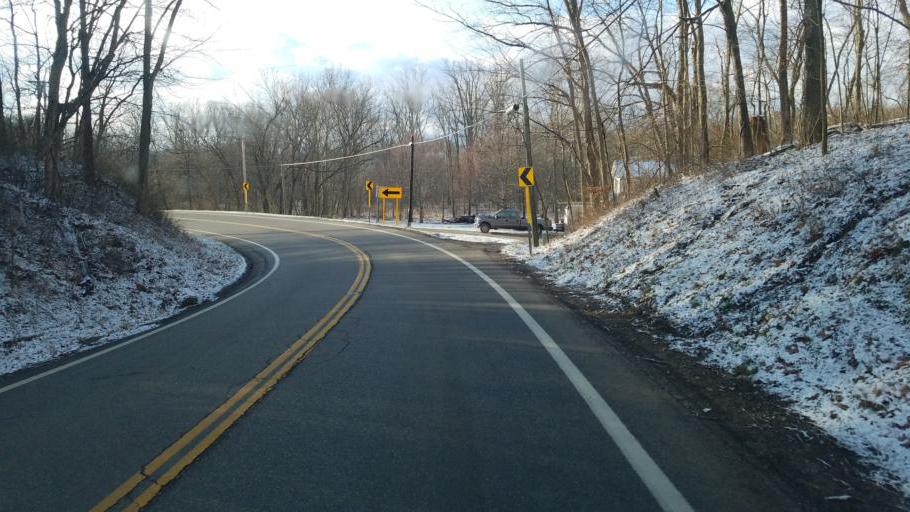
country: US
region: Ohio
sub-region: Ashland County
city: Loudonville
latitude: 40.6592
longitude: -82.1381
